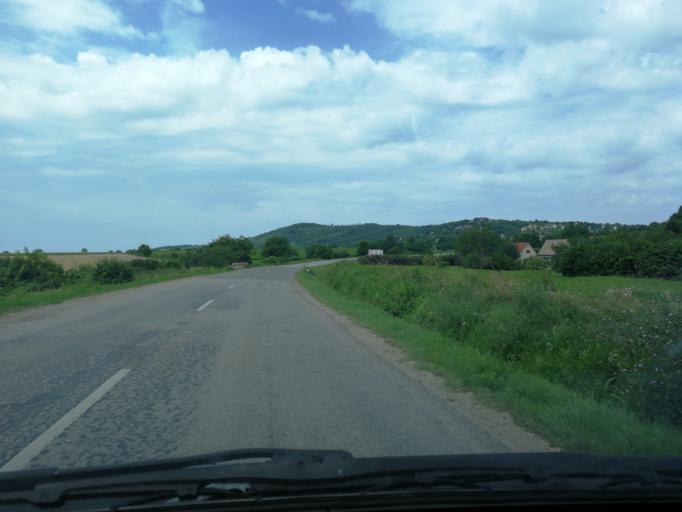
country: HU
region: Baranya
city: Harkany
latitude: 45.8760
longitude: 18.2466
